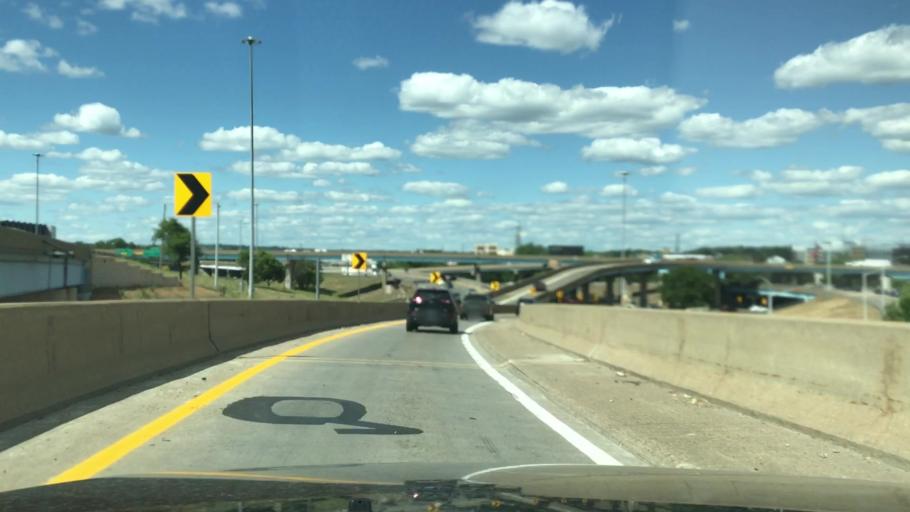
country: US
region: Michigan
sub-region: Kent County
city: Grand Rapids
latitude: 42.9708
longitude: -85.6779
